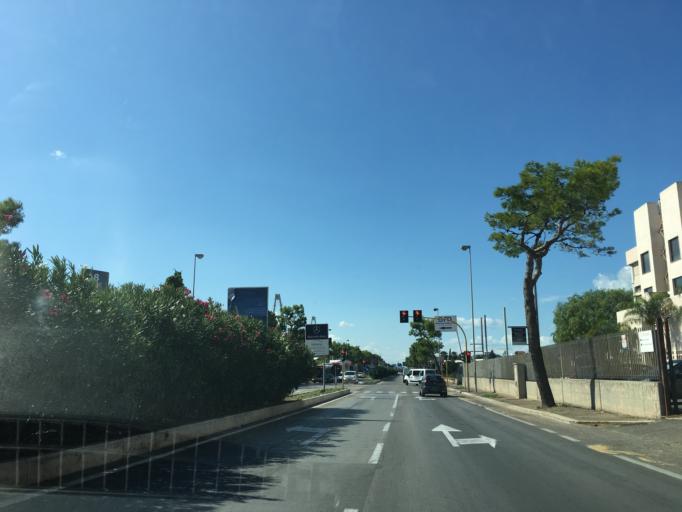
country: IT
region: Apulia
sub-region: Provincia di Bari
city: San Paolo
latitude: 41.1326
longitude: 16.8237
